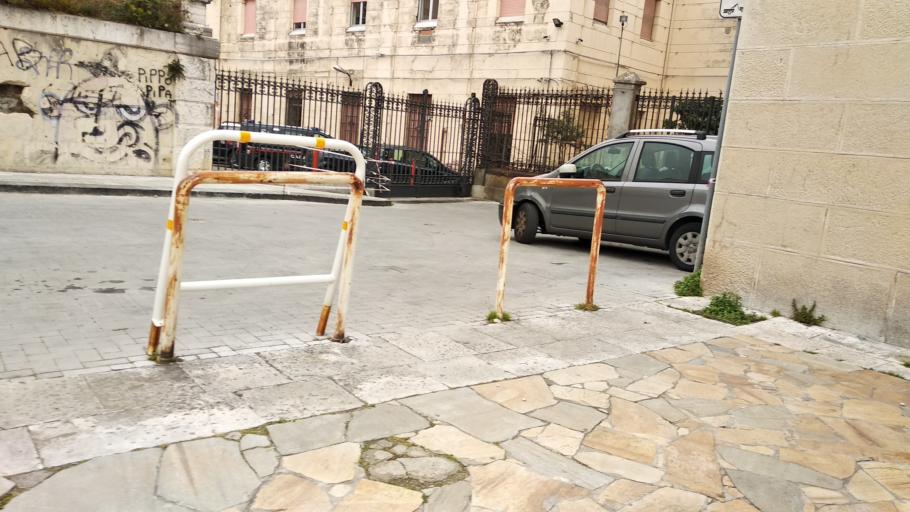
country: IT
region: Sicily
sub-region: Messina
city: Messina
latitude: 38.1984
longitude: 15.5534
